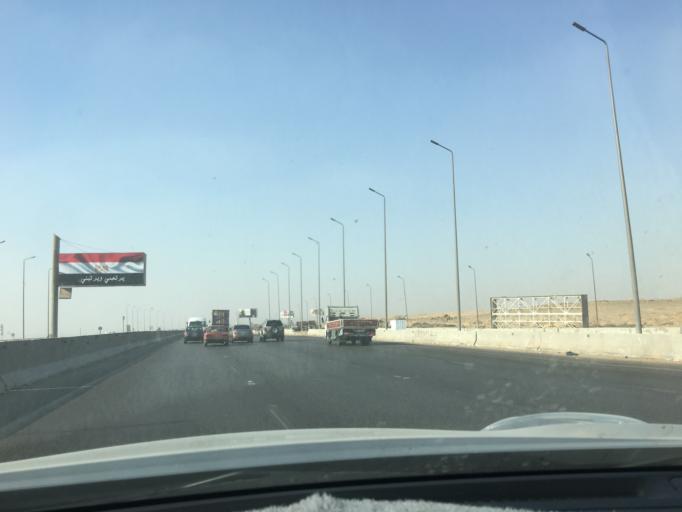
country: EG
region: Muhafazat al Qalyubiyah
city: Al Khankah
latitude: 30.0827
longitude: 31.4364
